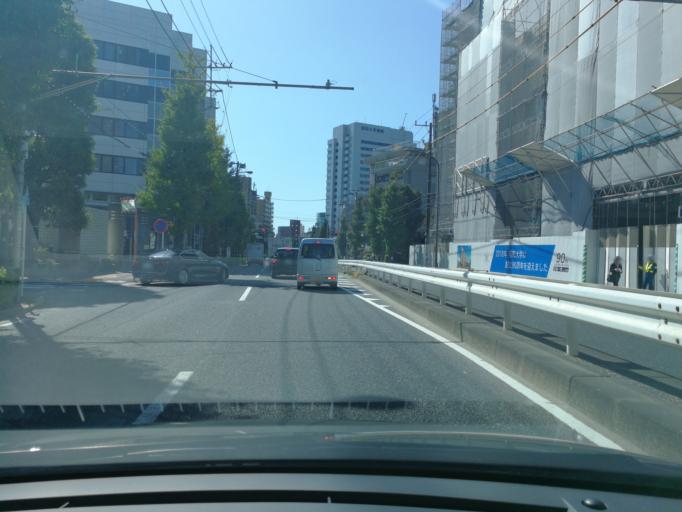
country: JP
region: Tokyo
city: Tokyo
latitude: 35.6102
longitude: 139.7055
